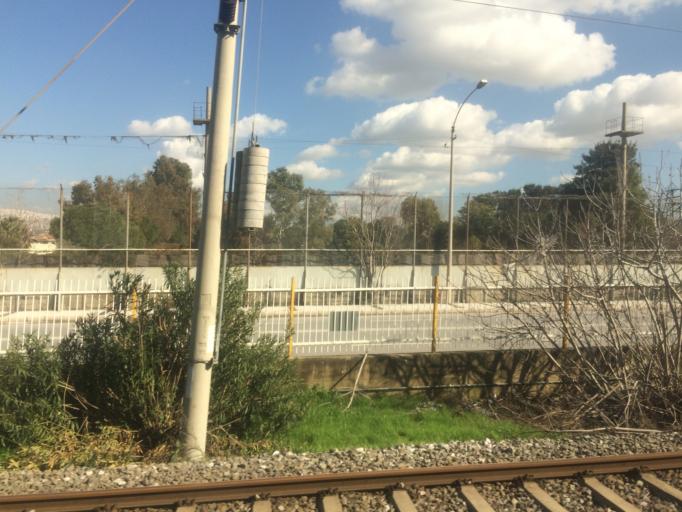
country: TR
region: Izmir
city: Izmir
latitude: 38.4578
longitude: 27.1684
